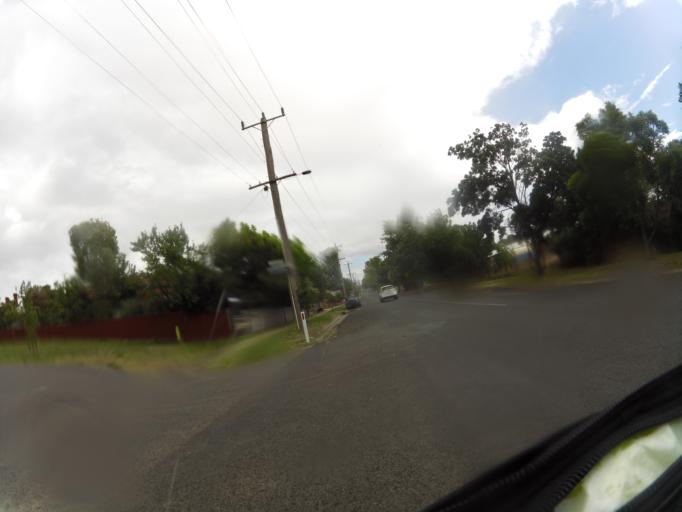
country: AU
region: Victoria
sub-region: Mount Alexander
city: Castlemaine
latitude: -37.0593
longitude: 144.2154
